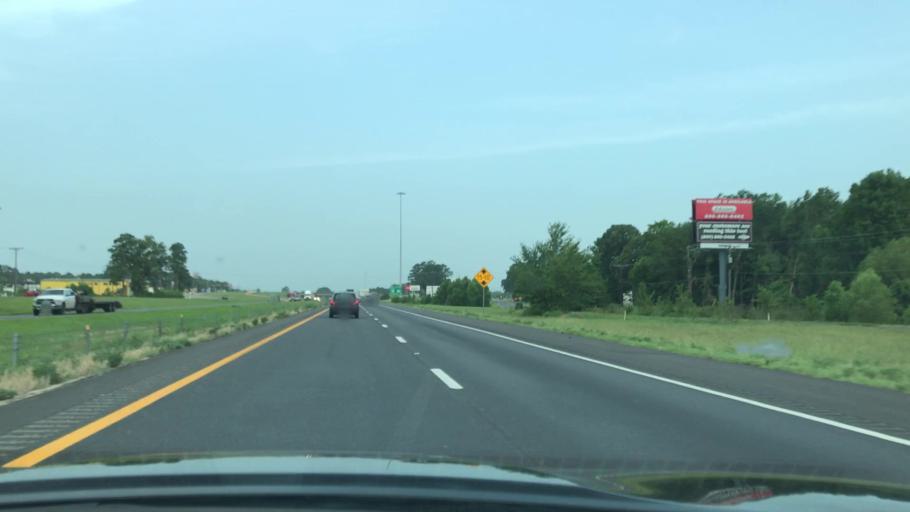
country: US
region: Texas
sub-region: Gregg County
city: Longview
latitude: 32.4614
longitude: -94.6592
